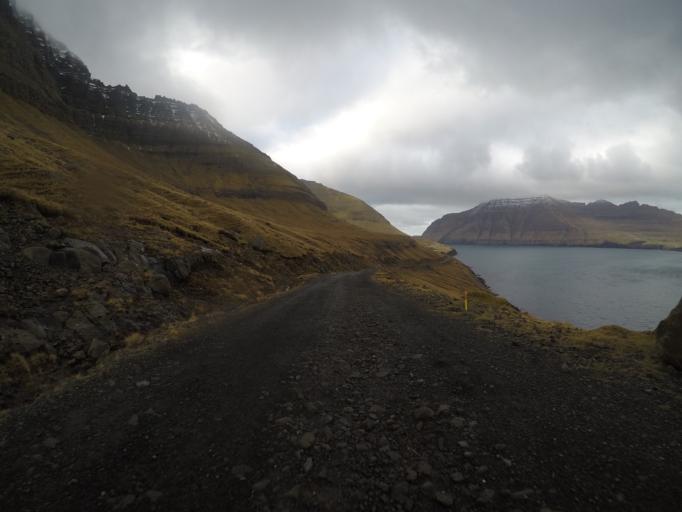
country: FO
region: Nordoyar
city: Klaksvik
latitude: 62.3385
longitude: -6.5798
